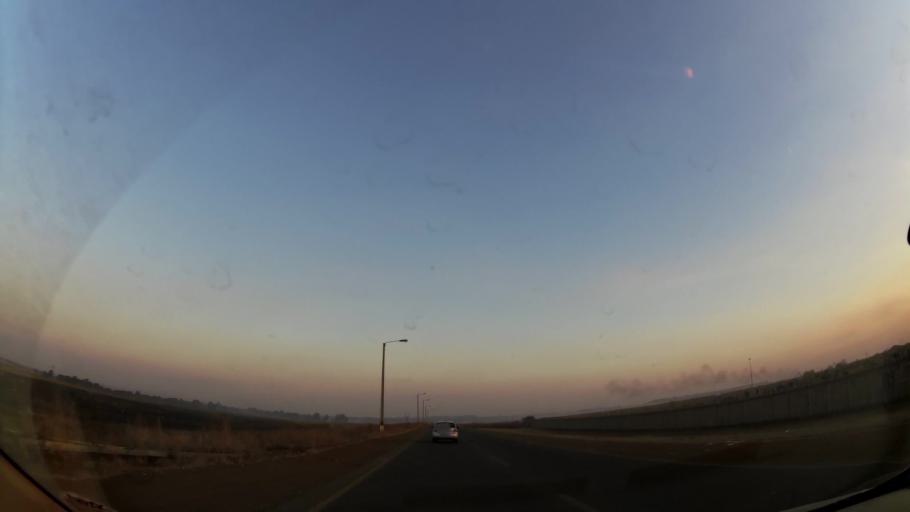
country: ZA
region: Gauteng
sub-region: Ekurhuleni Metropolitan Municipality
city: Springs
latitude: -26.3184
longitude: 28.4250
